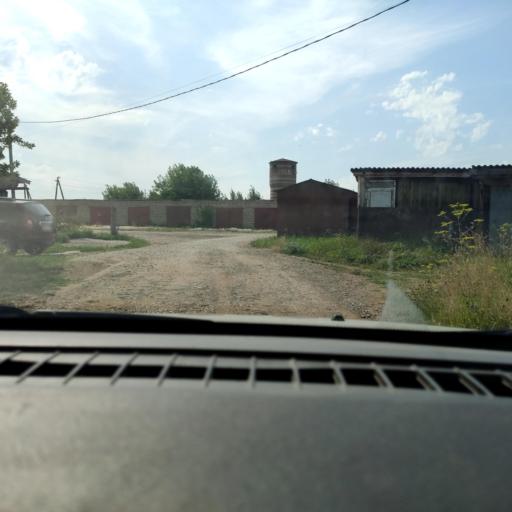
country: RU
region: Perm
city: Froly
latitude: 57.8877
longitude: 56.2508
